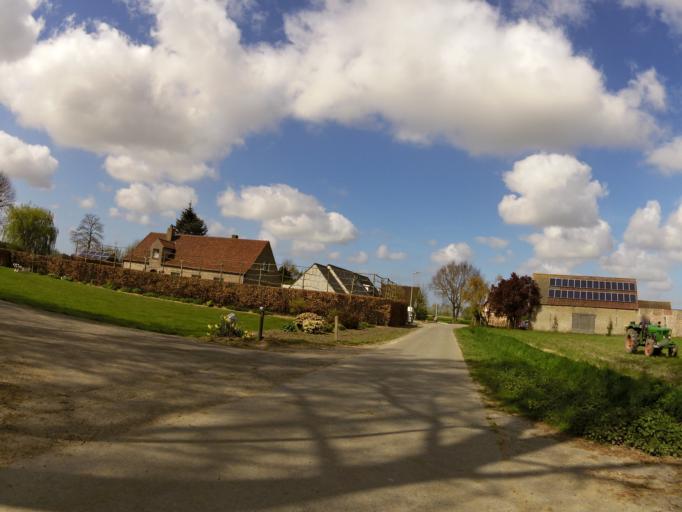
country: BE
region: Flanders
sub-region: Provincie West-Vlaanderen
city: Jabbeke
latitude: 51.1975
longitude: 3.1185
